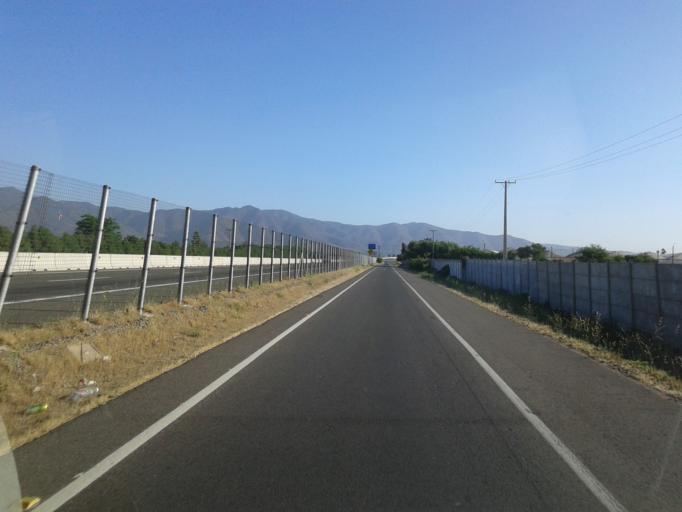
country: CL
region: Valparaiso
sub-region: Provincia de Quillota
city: Quillota
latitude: -32.8528
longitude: -71.2246
